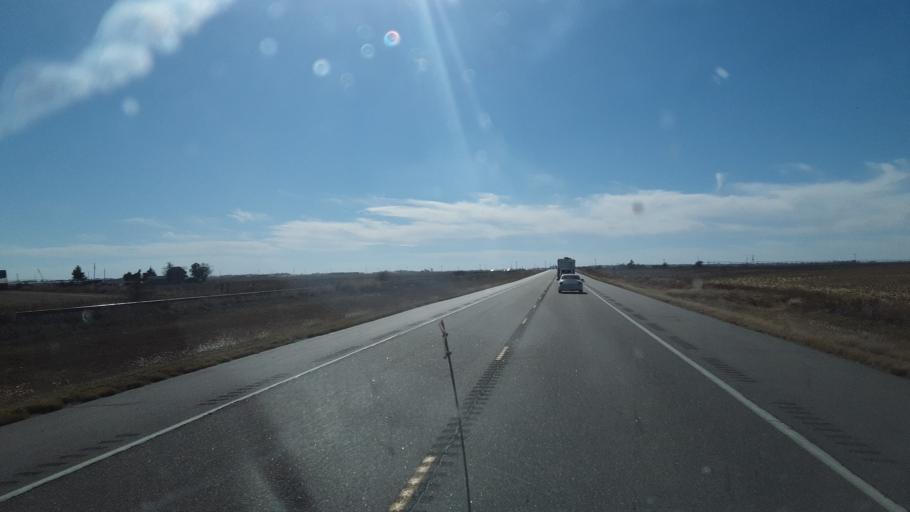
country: US
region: Kansas
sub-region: Pawnee County
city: Larned
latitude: 38.2287
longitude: -99.0348
